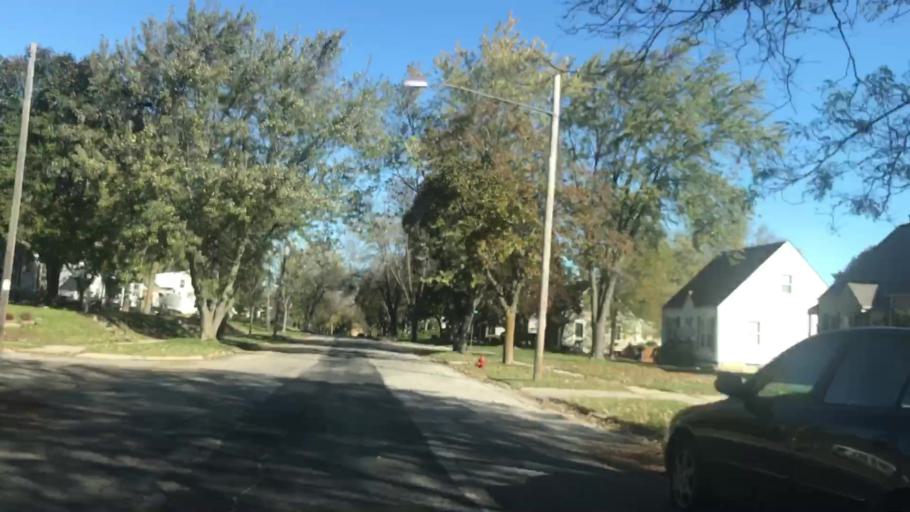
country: US
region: Wisconsin
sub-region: Waukesha County
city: Menomonee Falls
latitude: 43.1715
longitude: -88.1144
